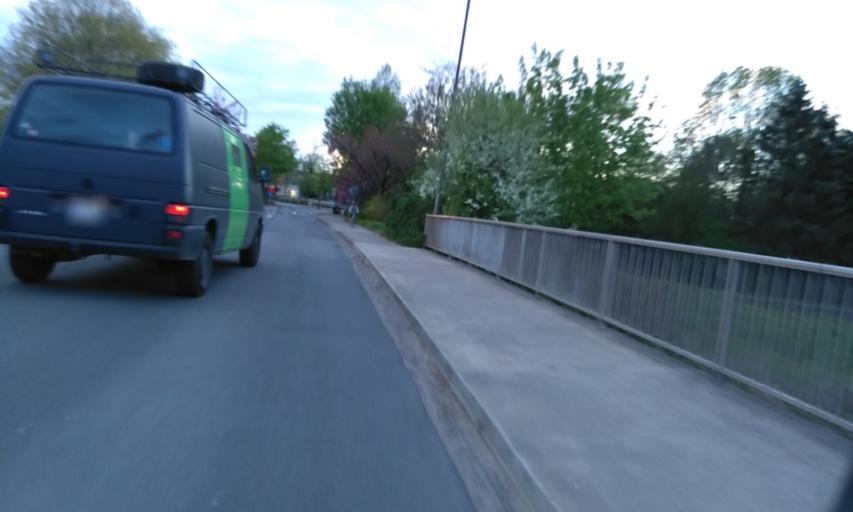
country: DE
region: Lower Saxony
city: Horneburg
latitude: 53.5065
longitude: 9.5858
